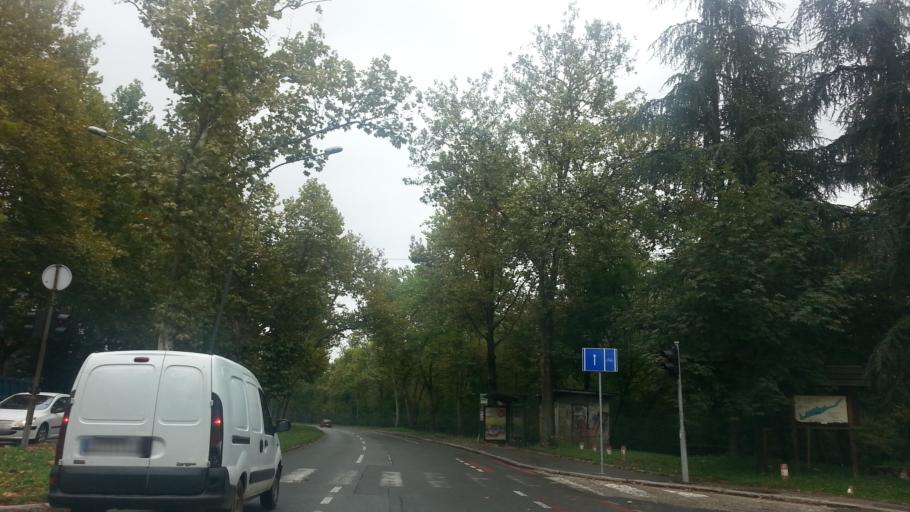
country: RS
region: Central Serbia
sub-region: Belgrade
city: Vozdovac
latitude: 44.7798
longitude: 20.4683
